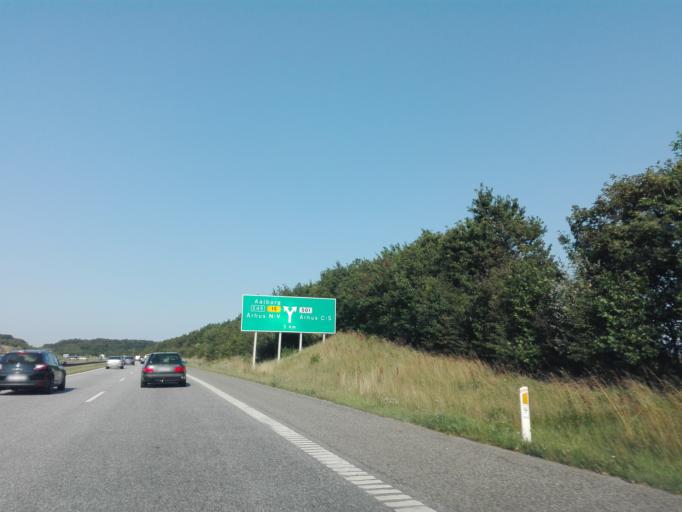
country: DK
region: Central Jutland
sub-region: Skanderborg Kommune
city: Stilling
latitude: 56.0769
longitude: 10.0037
